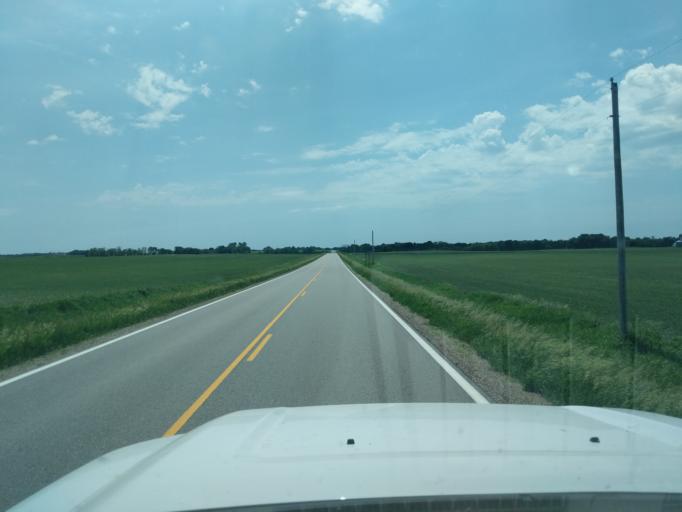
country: US
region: Minnesota
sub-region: Yellow Medicine County
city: Granite Falls
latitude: 44.7573
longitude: -95.4014
